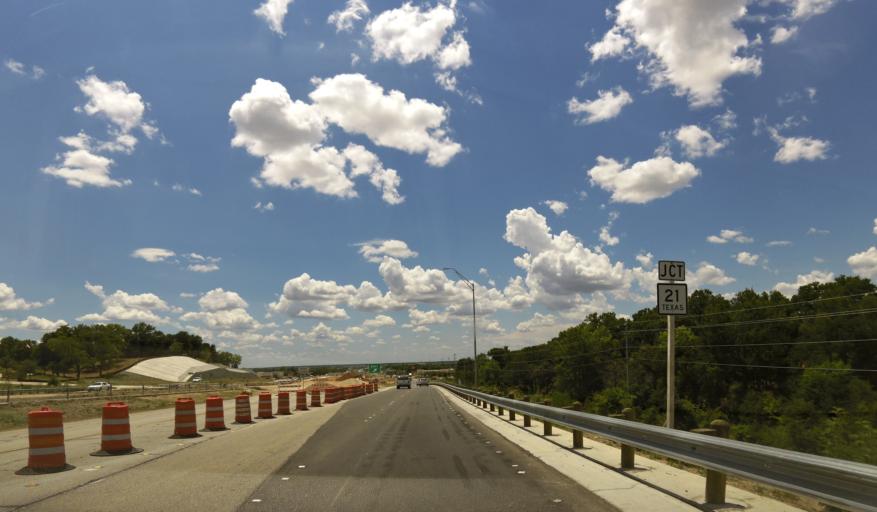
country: US
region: Texas
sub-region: Bastrop County
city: Bastrop
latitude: 30.1052
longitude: -97.3028
